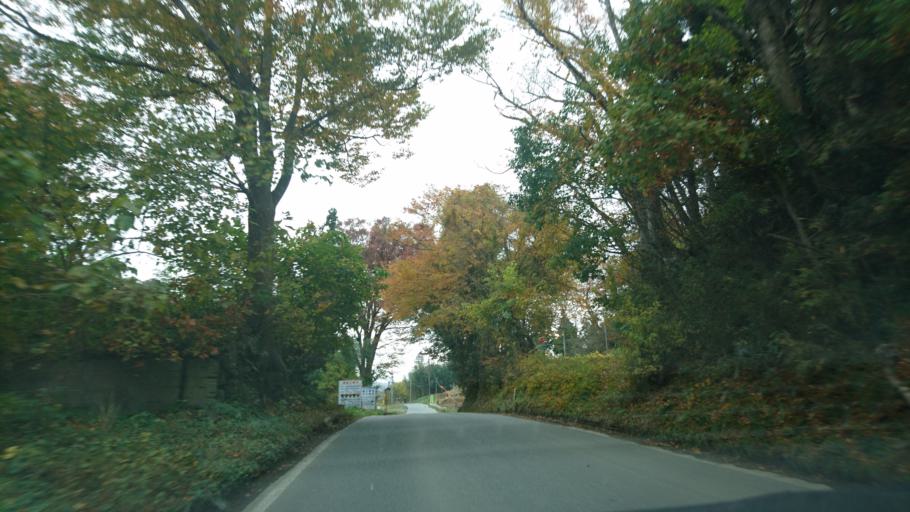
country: JP
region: Iwate
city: Ichinoseki
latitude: 38.9513
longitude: 141.1790
